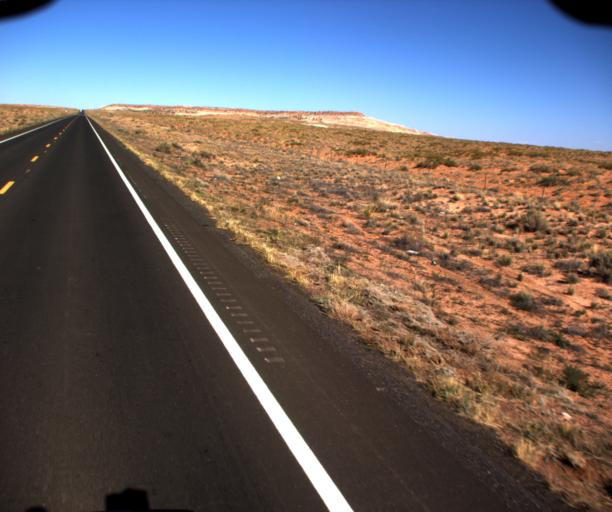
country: US
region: Arizona
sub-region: Coconino County
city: Tuba City
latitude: 36.2087
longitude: -111.0514
